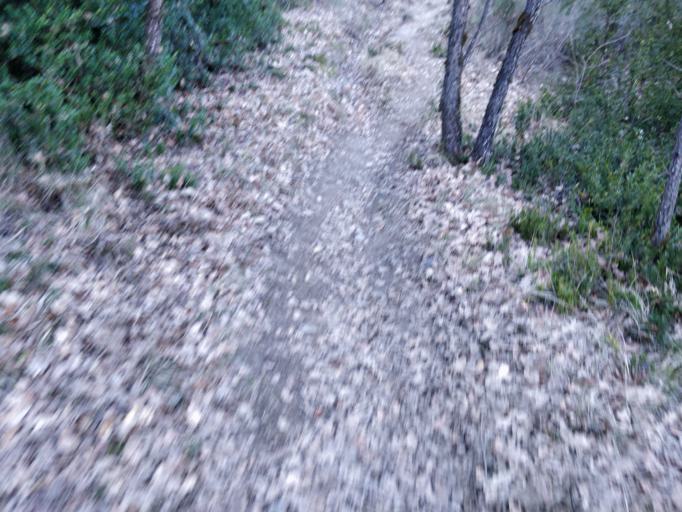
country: FR
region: Provence-Alpes-Cote d'Azur
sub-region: Departement des Alpes-de-Haute-Provence
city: Digne-les-Bains
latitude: 44.1024
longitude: 6.2457
